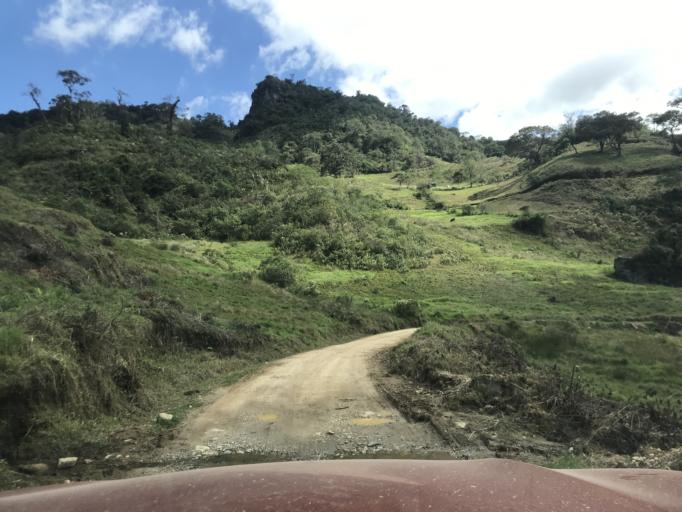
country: PE
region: Cajamarca
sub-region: Provincia de Chota
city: Querocoto
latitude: -6.3480
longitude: -79.0558
